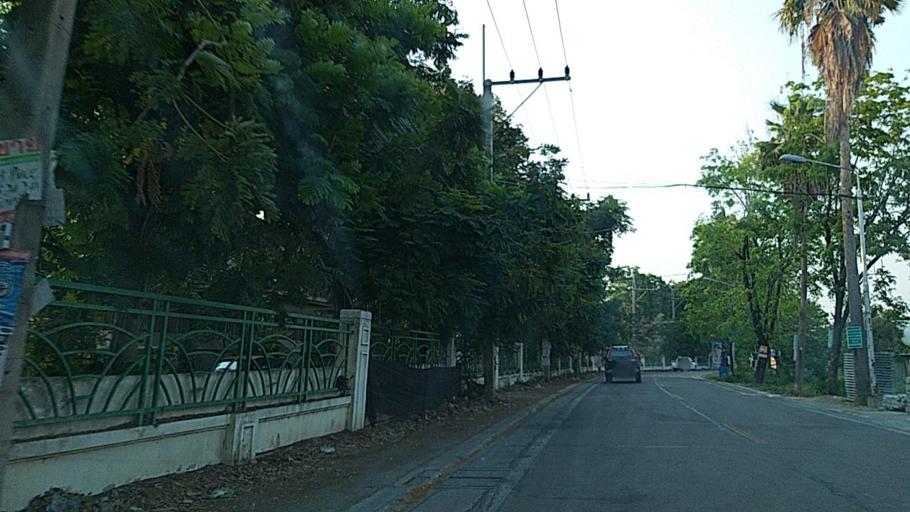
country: TH
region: Phra Nakhon Si Ayutthaya
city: Ban Bang Kadi Pathum Thani
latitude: 13.9993
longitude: 100.5640
